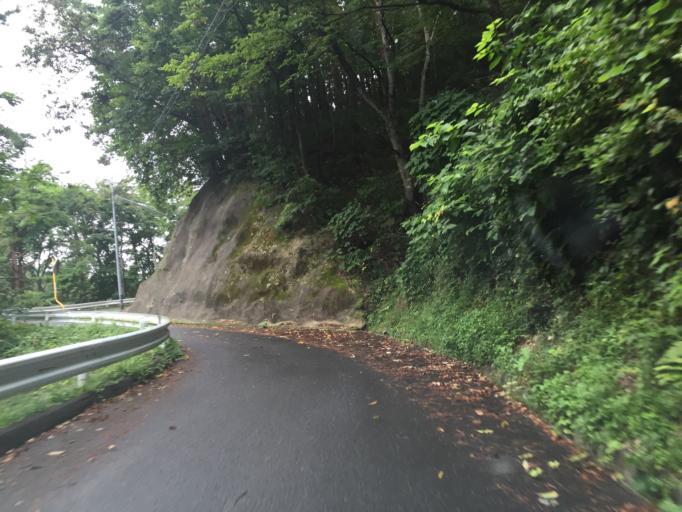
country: JP
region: Fukushima
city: Fukushima-shi
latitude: 37.8084
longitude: 140.3533
